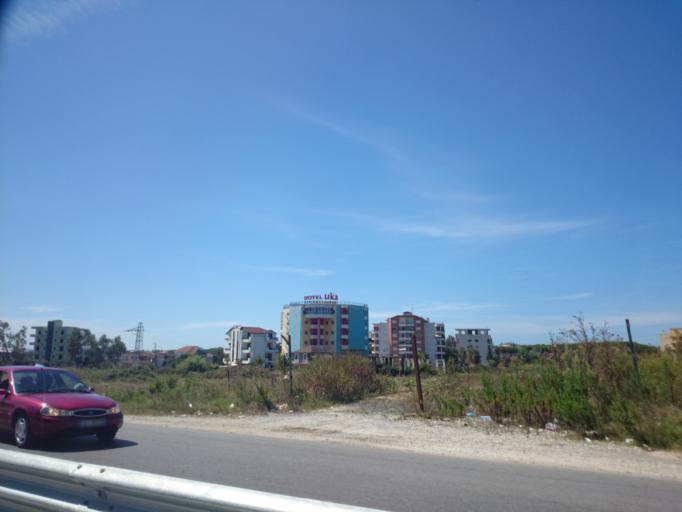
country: AL
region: Tirane
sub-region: Rrethi i Kavajes
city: Golem
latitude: 41.2340
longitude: 19.5239
